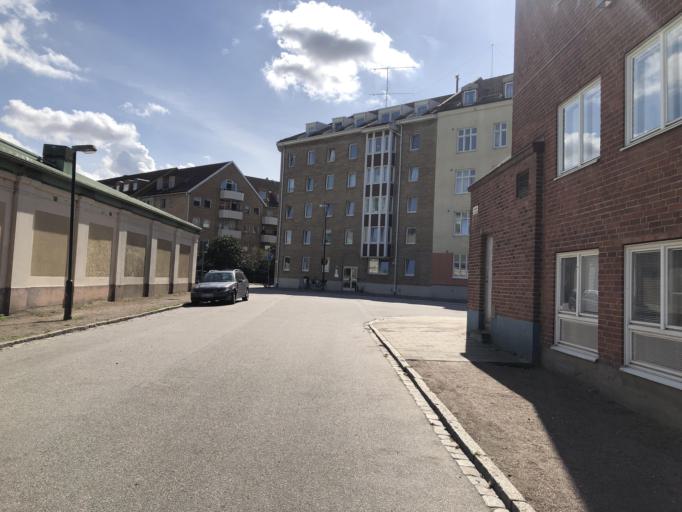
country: SE
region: Skane
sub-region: Burlovs Kommun
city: Arloev
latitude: 55.6112
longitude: 13.0391
